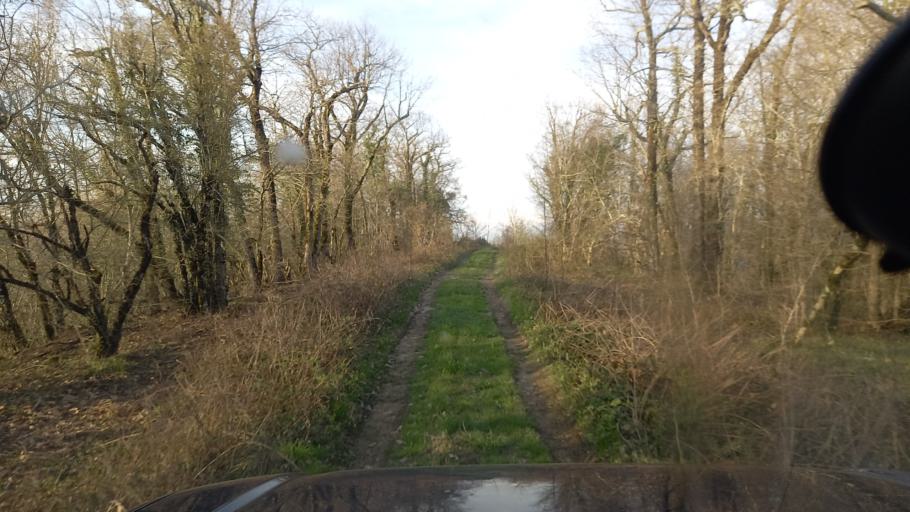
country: RU
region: Krasnodarskiy
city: Arkhipo-Osipovka
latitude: 44.3590
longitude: 38.5530
